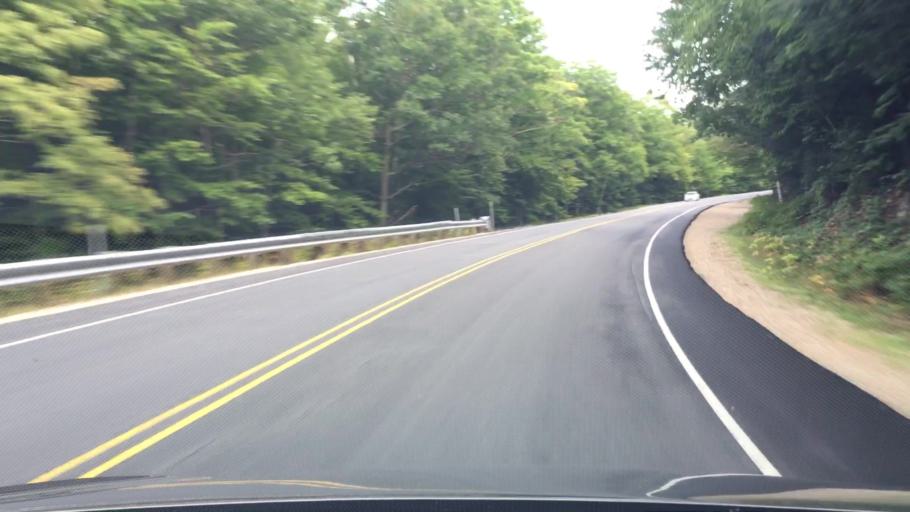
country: US
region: New Hampshire
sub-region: Carroll County
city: Conway
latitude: 44.0010
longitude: -71.2328
